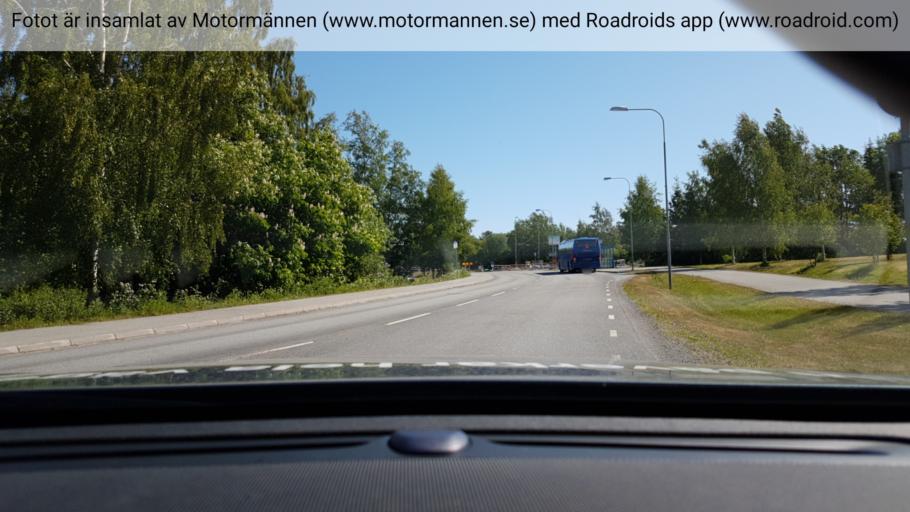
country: SE
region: Vaesterbotten
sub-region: Umea Kommun
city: Holmsund
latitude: 63.7057
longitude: 20.3618
